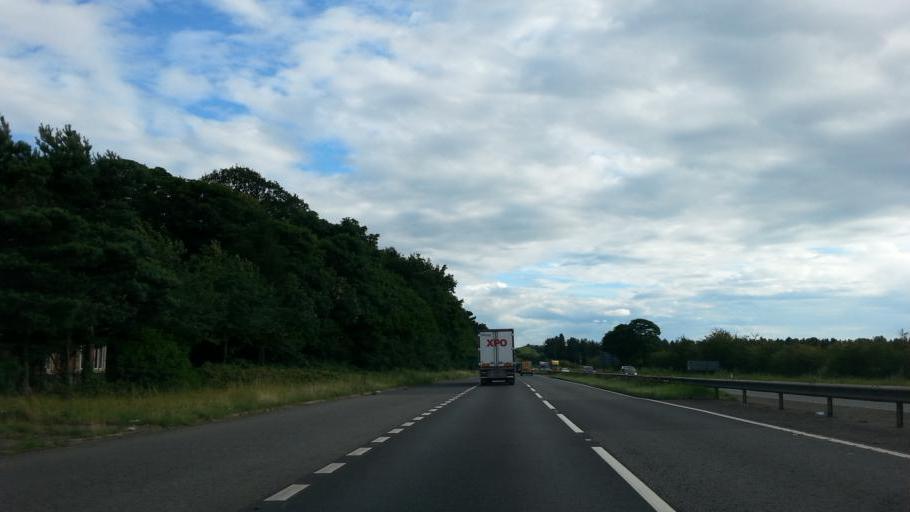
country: GB
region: England
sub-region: Nottinghamshire
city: Babworth
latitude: 53.3151
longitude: -1.0287
